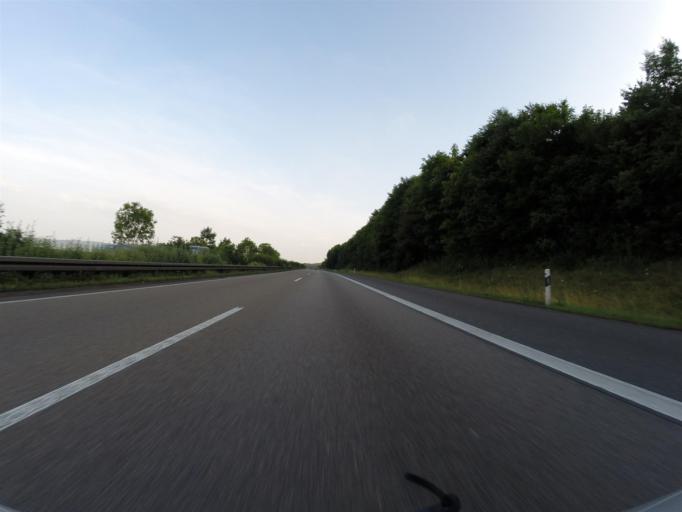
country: DE
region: Hesse
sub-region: Regierungsbezirk Kassel
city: Zierenberg
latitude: 51.3510
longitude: 9.2799
